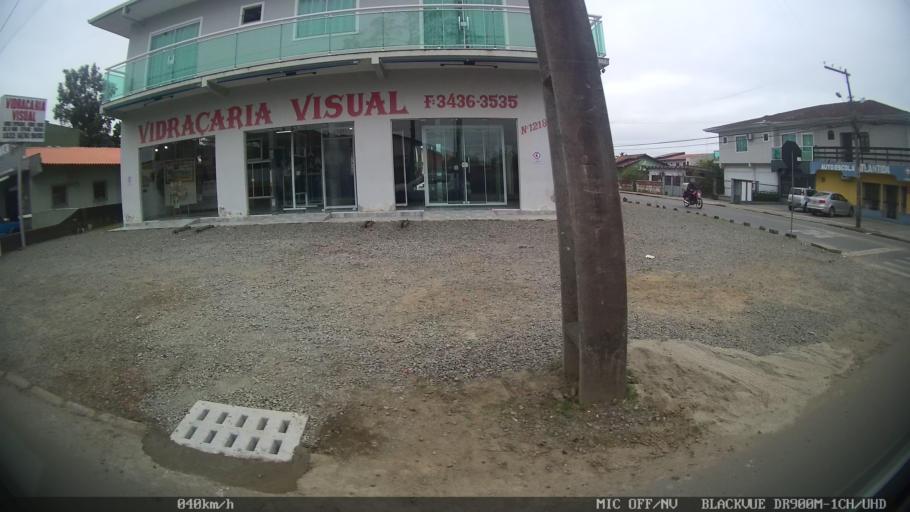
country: BR
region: Santa Catarina
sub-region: Joinville
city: Joinville
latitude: -26.3291
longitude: -48.8174
